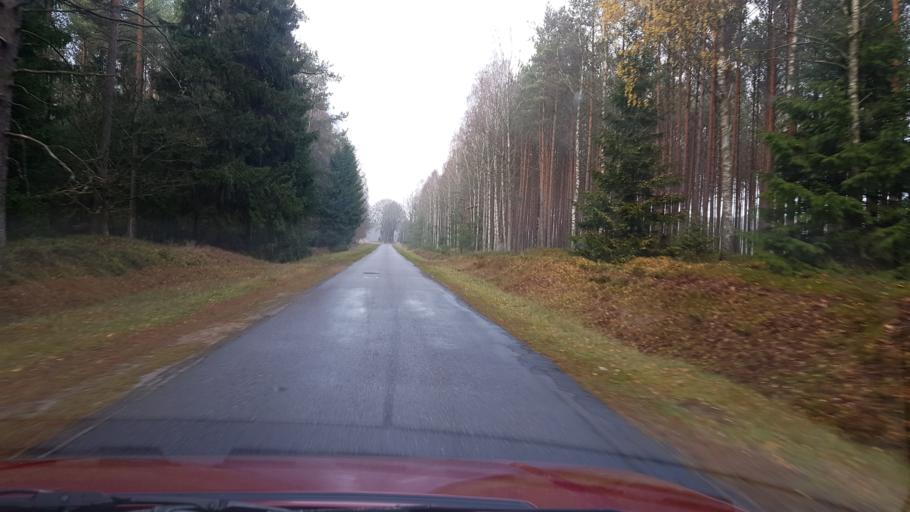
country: PL
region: West Pomeranian Voivodeship
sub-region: Powiat bialogardzki
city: Tychowo
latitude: 53.9609
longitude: 16.3180
